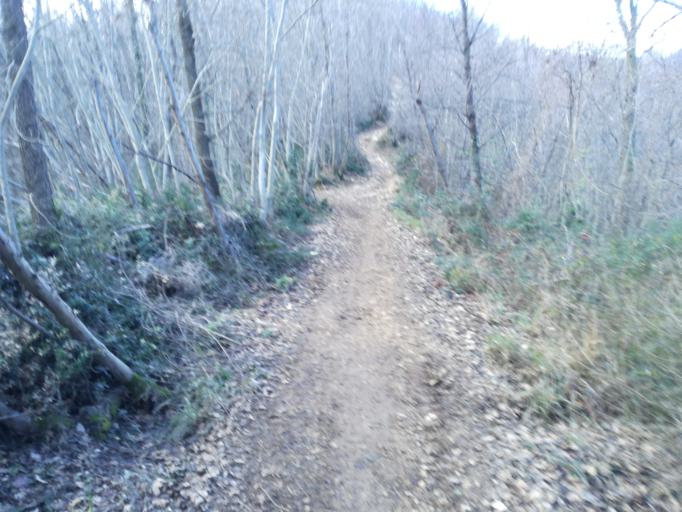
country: IT
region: Veneto
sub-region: Provincia di Padova
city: Galzignano
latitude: 45.2978
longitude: 11.7149
